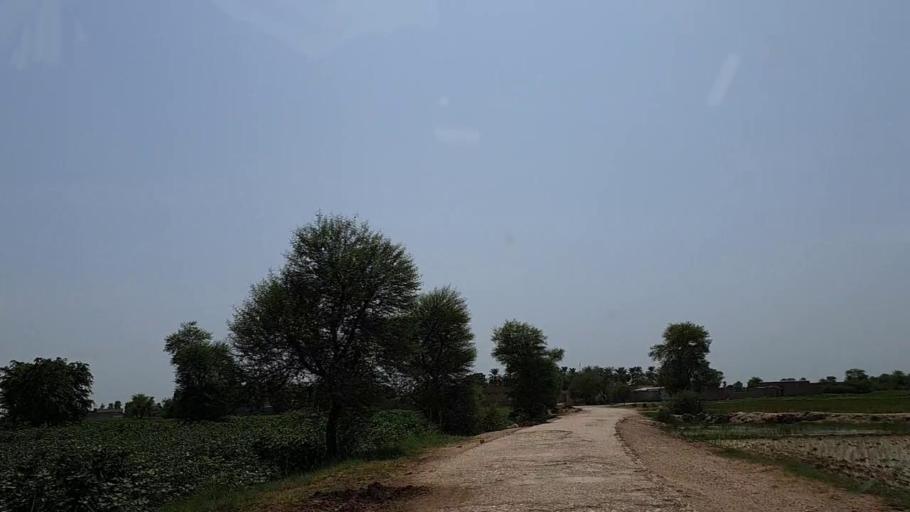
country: PK
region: Sindh
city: Adilpur
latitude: 27.9676
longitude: 69.3897
